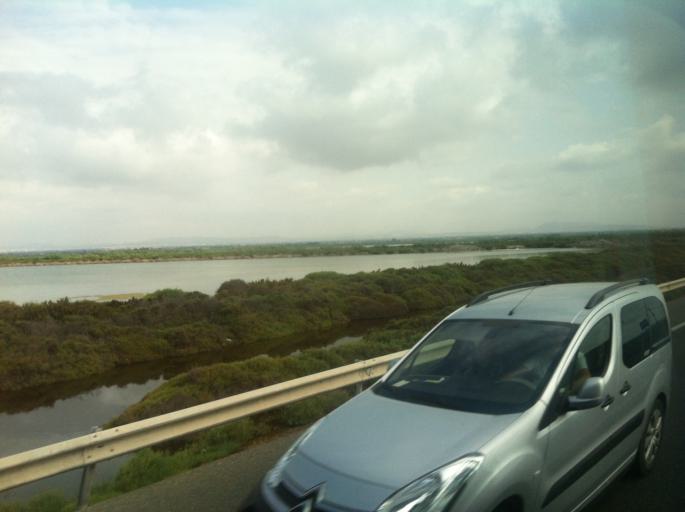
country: ES
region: Valencia
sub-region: Provincia de Alicante
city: Santa Pola
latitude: 38.1816
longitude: -0.6173
